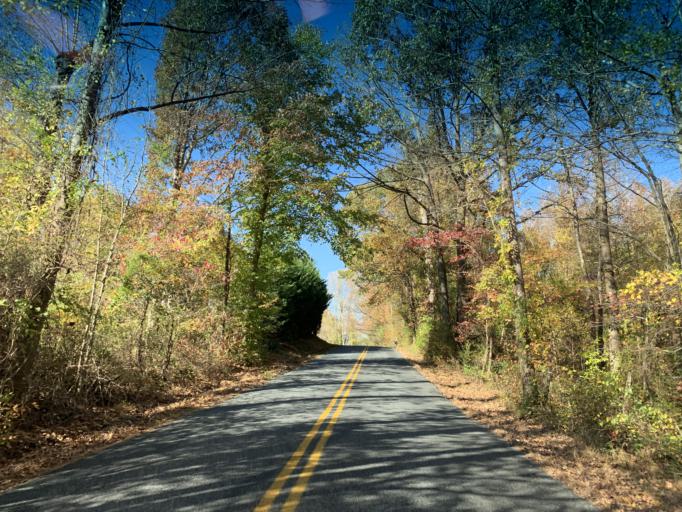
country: US
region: Maryland
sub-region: Harford County
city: Joppatowne
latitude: 39.4640
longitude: -76.3424
